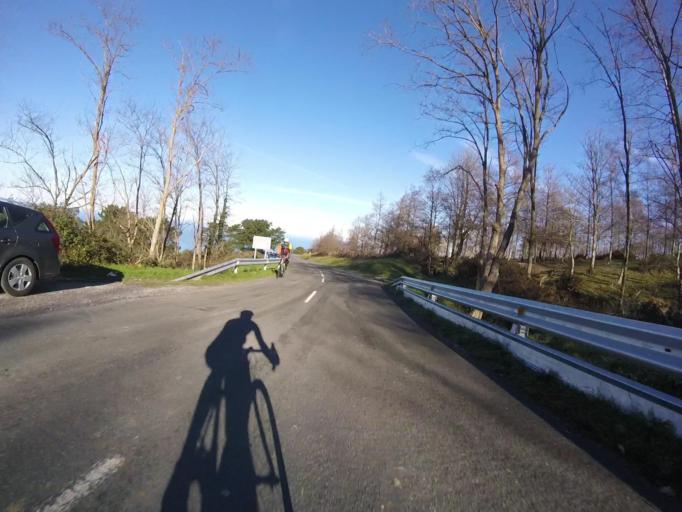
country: ES
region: Basque Country
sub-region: Provincia de Guipuzcoa
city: Fuenterrabia
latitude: 43.3622
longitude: -1.8344
